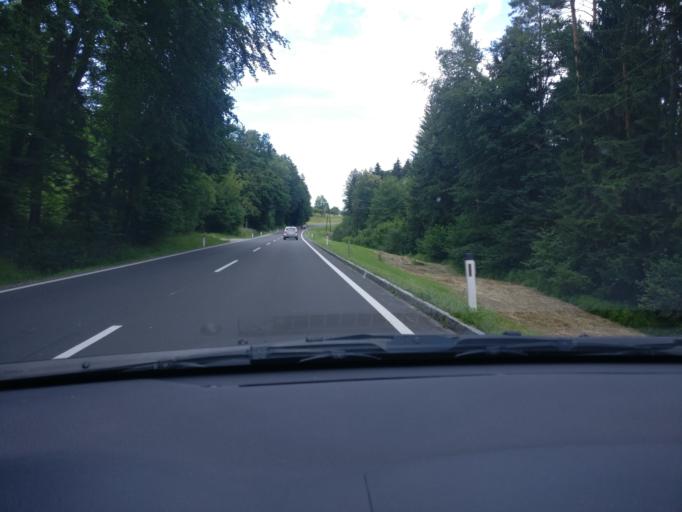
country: AT
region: Styria
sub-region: Politischer Bezirk Weiz
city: Oberrettenbach
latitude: 47.1616
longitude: 15.7755
